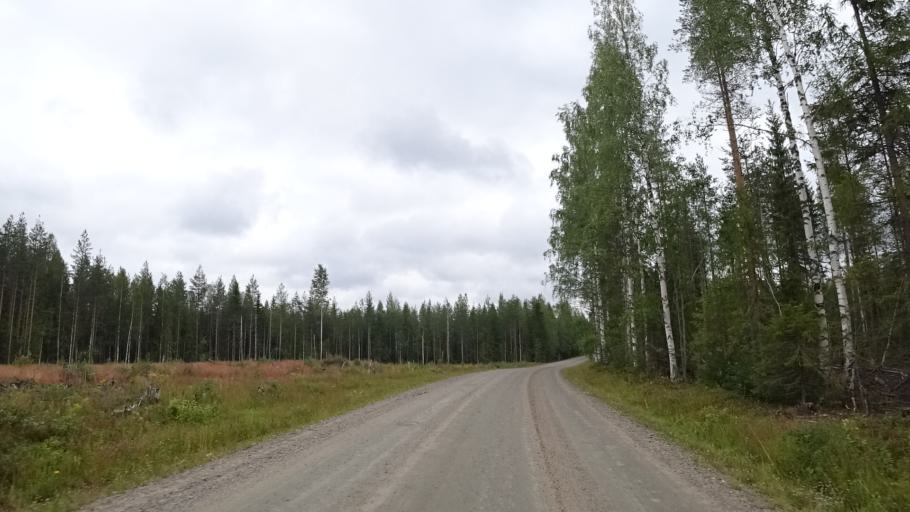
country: FI
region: North Karelia
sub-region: Joensuu
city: Ilomantsi
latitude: 63.0220
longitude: 31.2311
